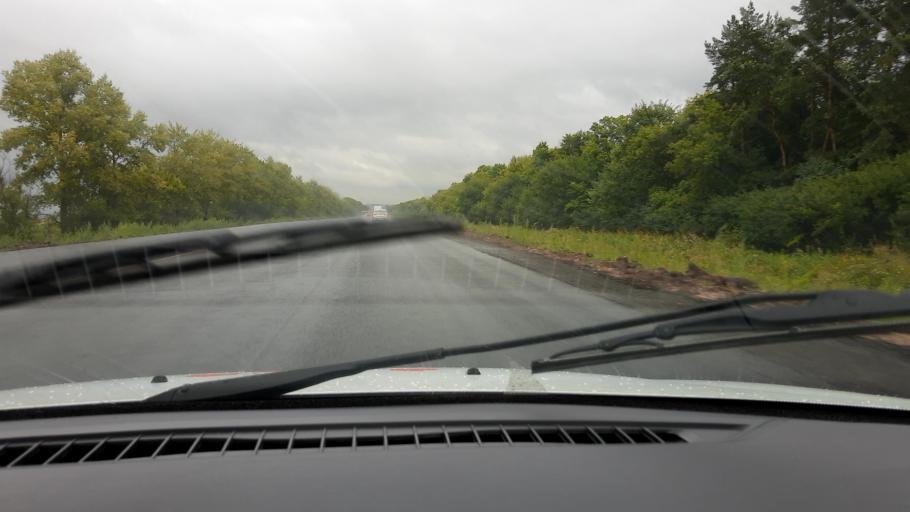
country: RU
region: Chuvashia
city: Yantikovo
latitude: 55.8008
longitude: 47.8729
